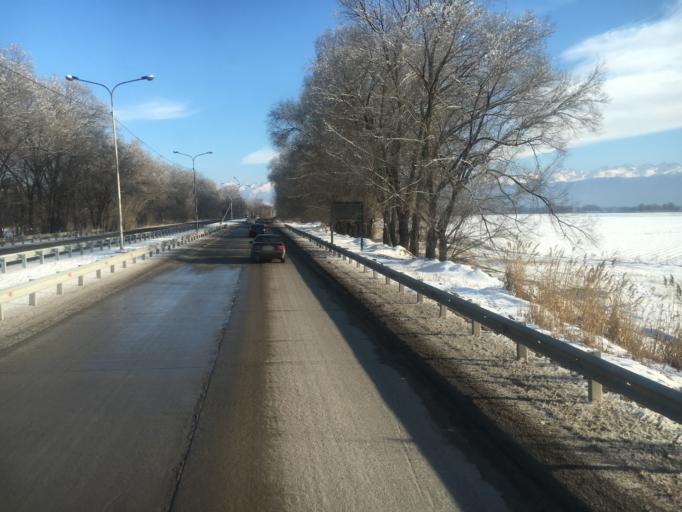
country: KZ
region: Almaty Oblysy
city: Burunday
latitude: 43.2737
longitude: 76.2936
